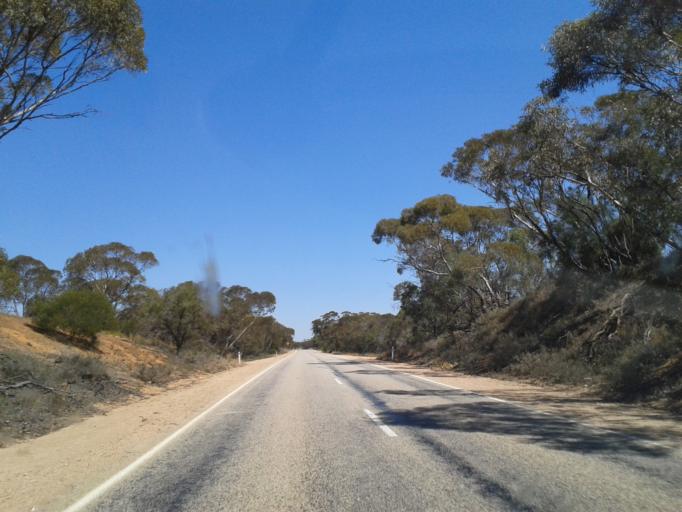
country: AU
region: Victoria
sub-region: Swan Hill
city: Swan Hill
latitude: -34.8365
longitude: 143.2623
